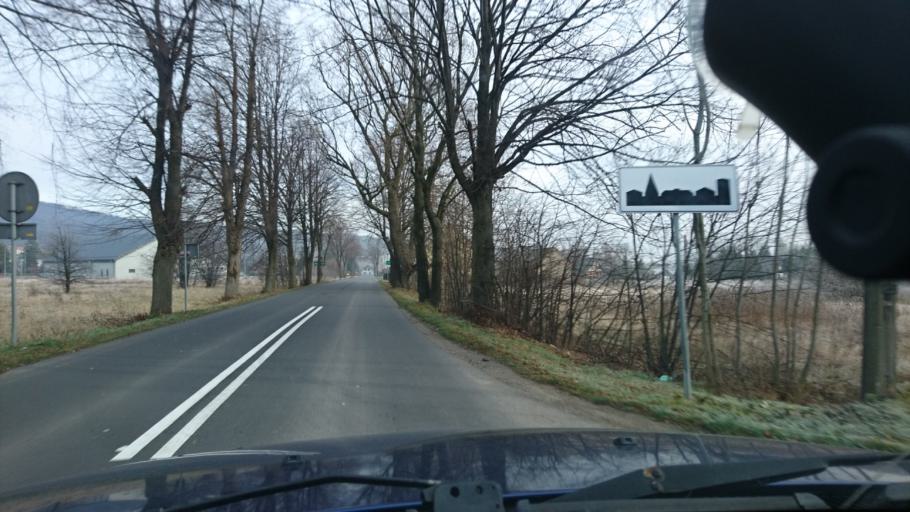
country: PL
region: Silesian Voivodeship
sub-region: Powiat zywiecki
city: Lodygowice
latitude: 49.7286
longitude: 19.1259
